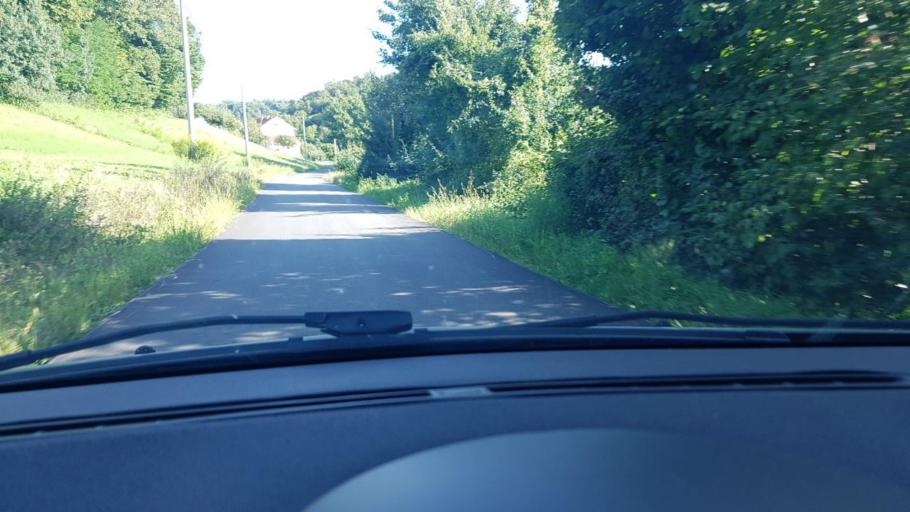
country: HR
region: Krapinsko-Zagorska
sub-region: Grad Krapina
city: Krapina
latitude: 46.1296
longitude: 15.8418
